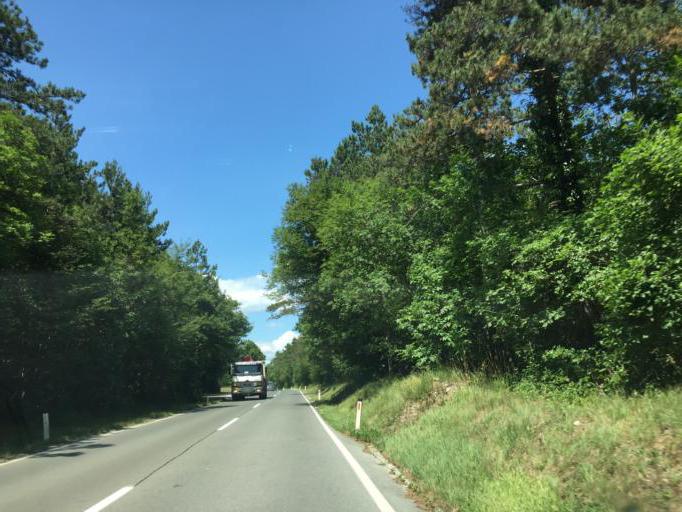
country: SI
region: Sezana
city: Sezana
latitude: 45.7322
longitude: 13.8673
